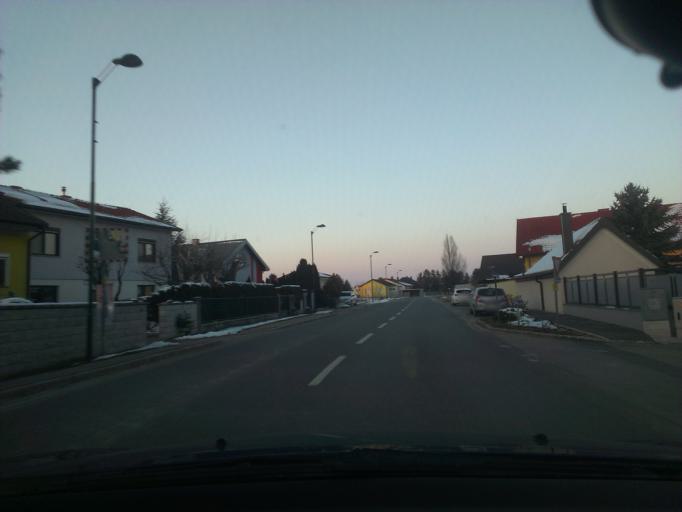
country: AT
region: Lower Austria
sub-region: Politischer Bezirk Bruck an der Leitha
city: Gotzendorf an der Leitha
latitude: 48.0086
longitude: 16.5684
